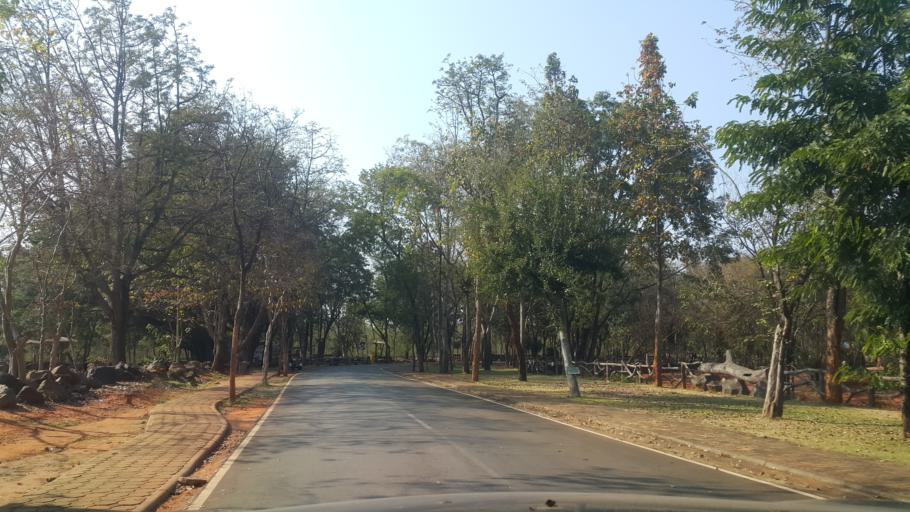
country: TH
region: Nakhon Ratchasima
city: Nakhon Ratchasima
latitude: 14.8549
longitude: 102.0869
